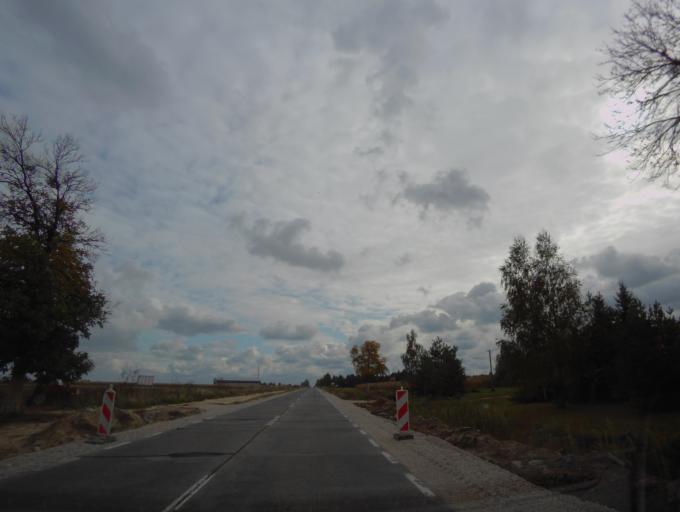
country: PL
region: Lublin Voivodeship
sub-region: Powiat wlodawski
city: Wlodawa
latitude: 51.5617
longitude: 23.5178
